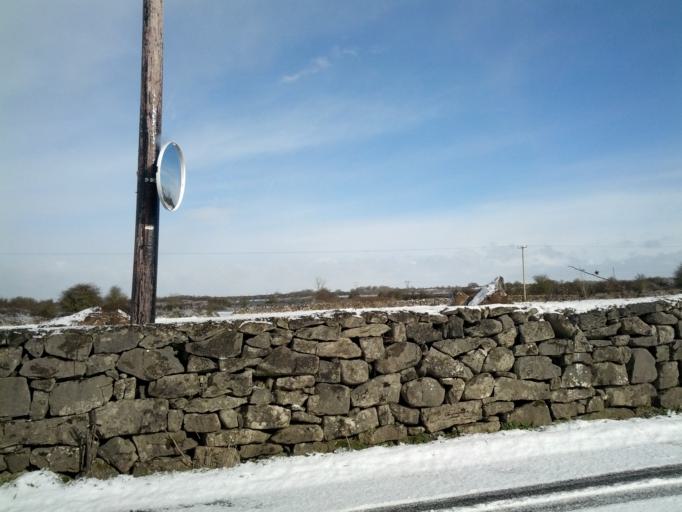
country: IE
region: Connaught
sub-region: County Galway
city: Oranmore
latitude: 53.1840
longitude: -8.9065
